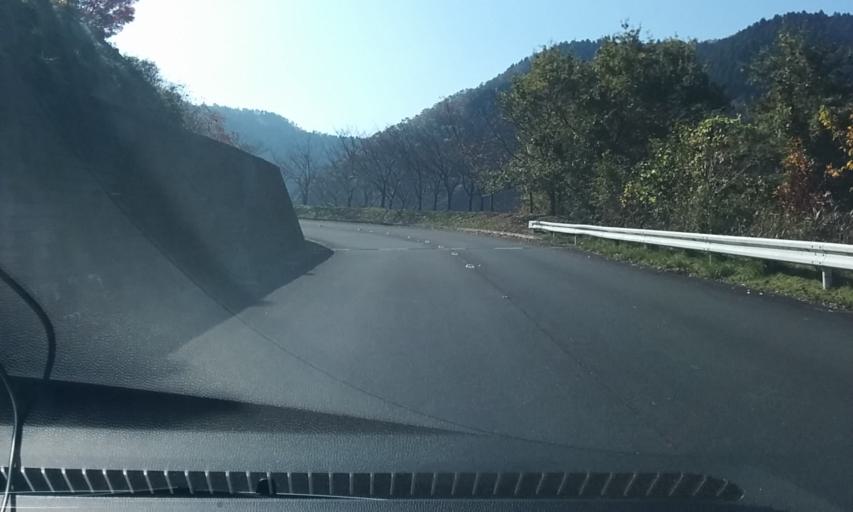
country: JP
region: Kyoto
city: Kameoka
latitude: 35.1495
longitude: 135.5195
